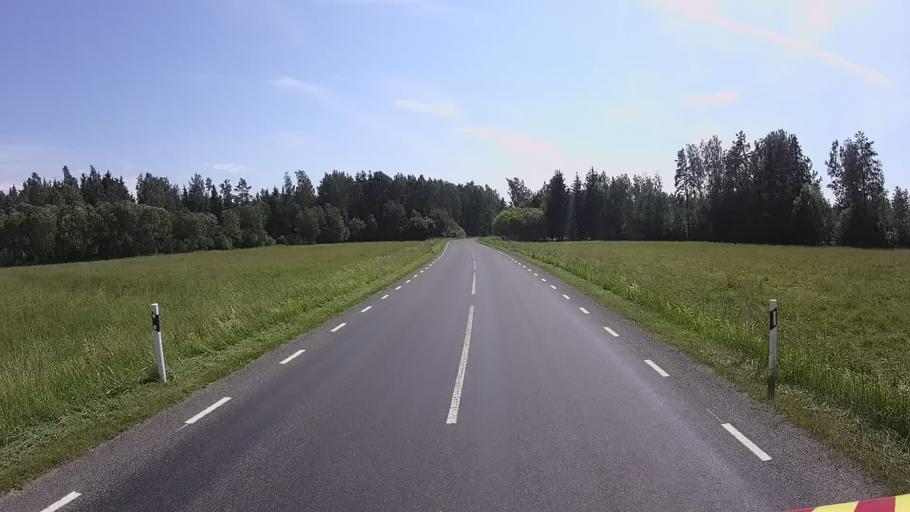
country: EE
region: Viljandimaa
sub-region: Karksi vald
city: Karksi-Nuia
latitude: 58.0556
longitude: 25.5481
